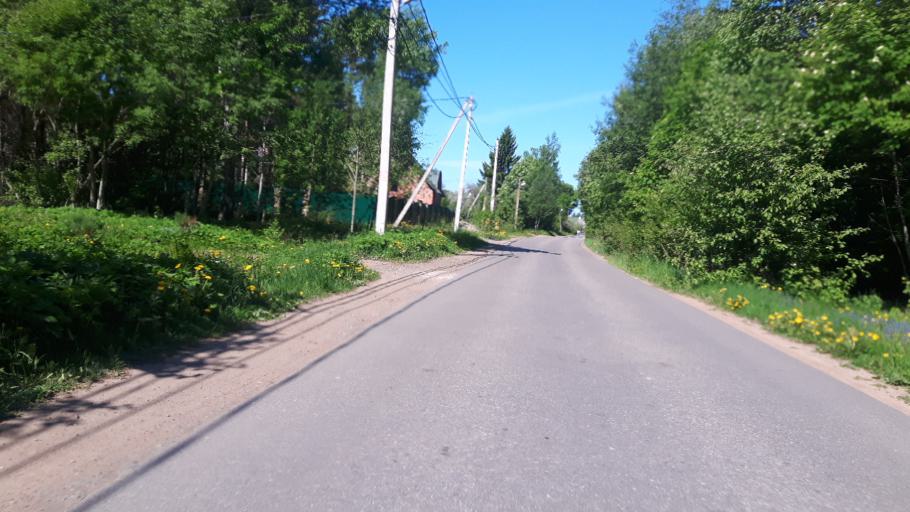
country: RU
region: Leningrad
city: Lebyazh'ye
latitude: 59.9706
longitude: 29.3856
